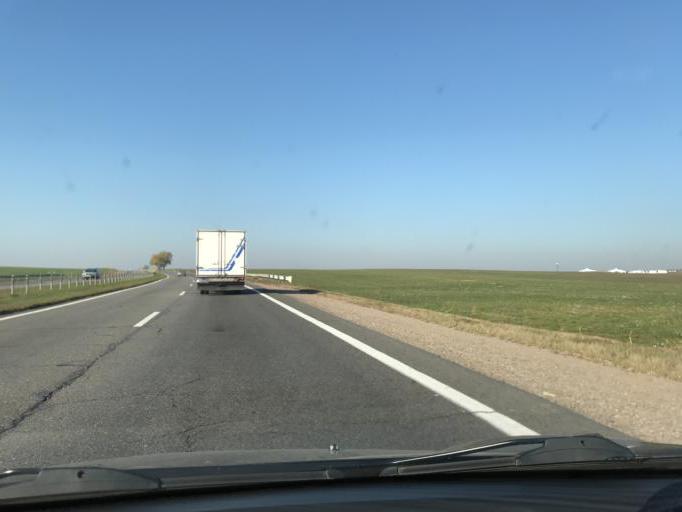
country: BY
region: Minsk
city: Dukora
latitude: 53.6760
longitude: 27.9302
